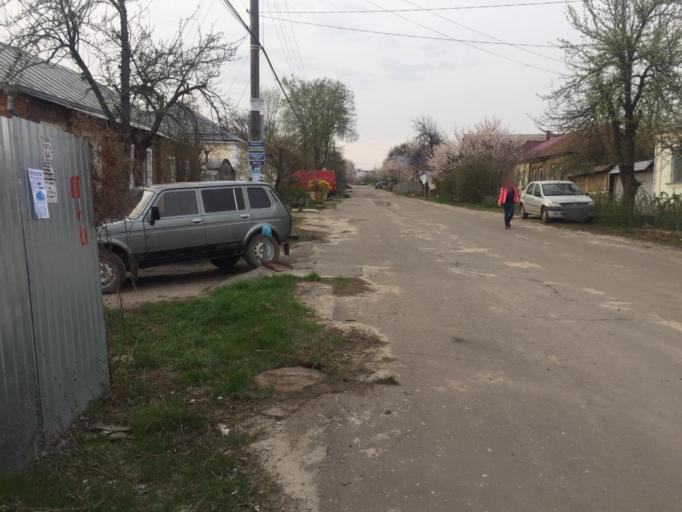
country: RU
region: Voronezj
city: Voronezh
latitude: 51.6949
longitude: 39.1584
